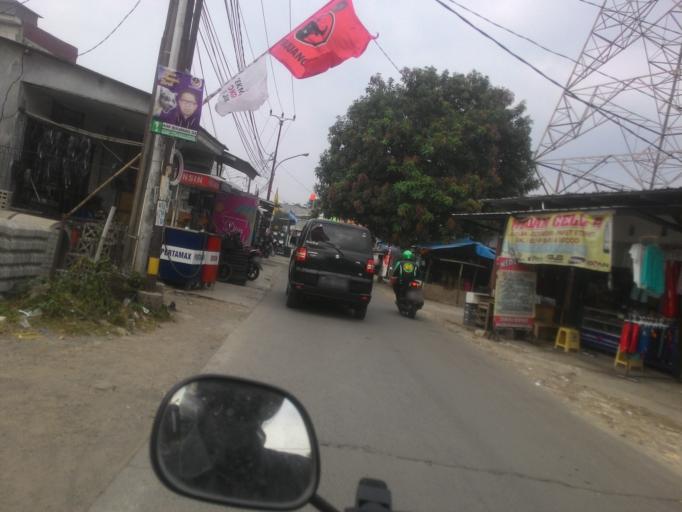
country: ID
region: West Java
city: Depok
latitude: -6.4216
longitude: 106.8386
